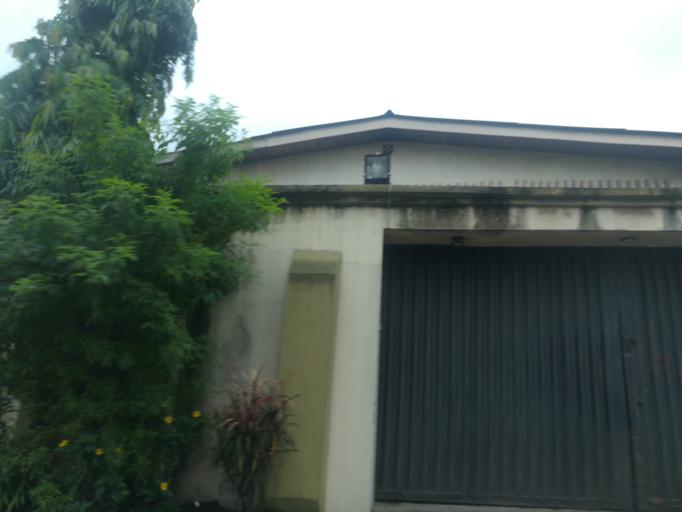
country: NG
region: Lagos
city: Ojota
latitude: 6.5748
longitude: 3.3732
